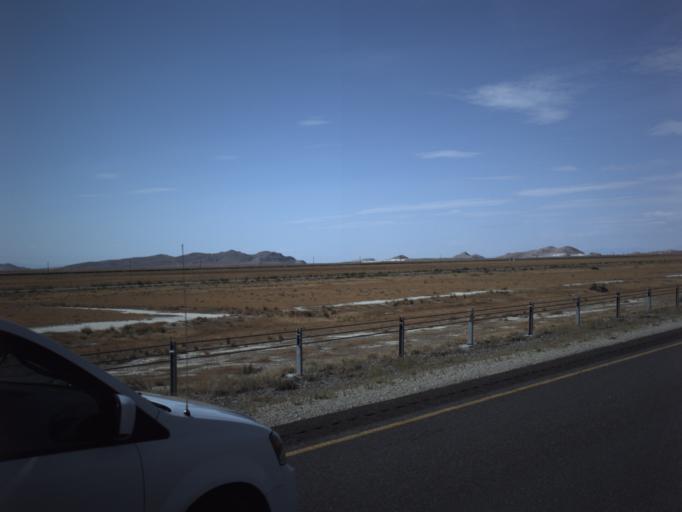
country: US
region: Utah
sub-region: Tooele County
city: Grantsville
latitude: 40.7269
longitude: -113.2188
